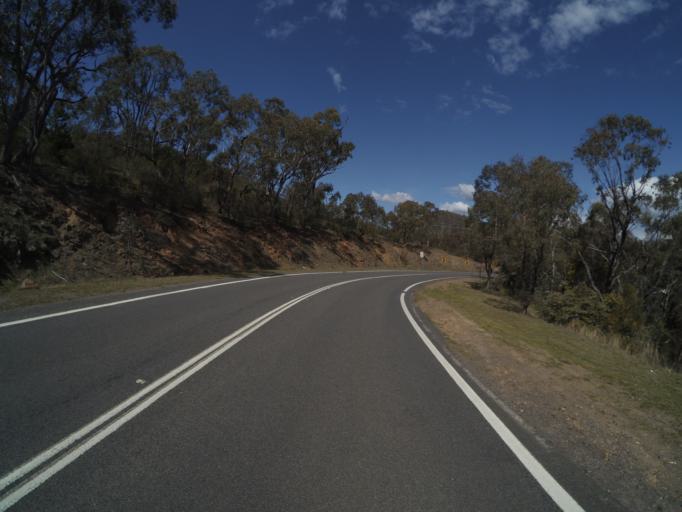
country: AU
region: Australian Capital Territory
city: Macquarie
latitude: -35.3230
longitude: 148.9442
